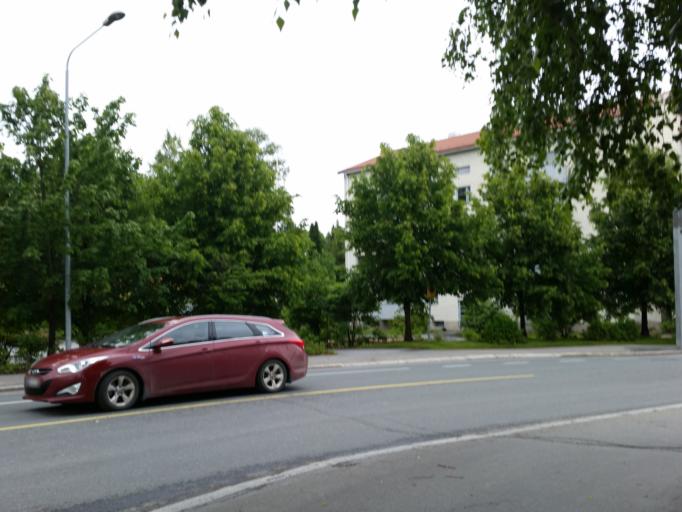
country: FI
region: Northern Savo
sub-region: Kuopio
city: Kuopio
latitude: 62.8964
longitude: 27.6706
